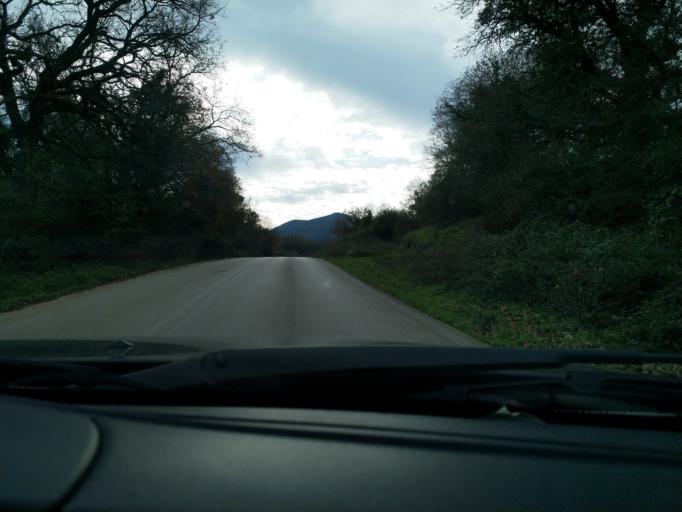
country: GR
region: Epirus
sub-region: Nomos Prevezis
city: Filippiada
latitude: 39.2274
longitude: 20.8439
